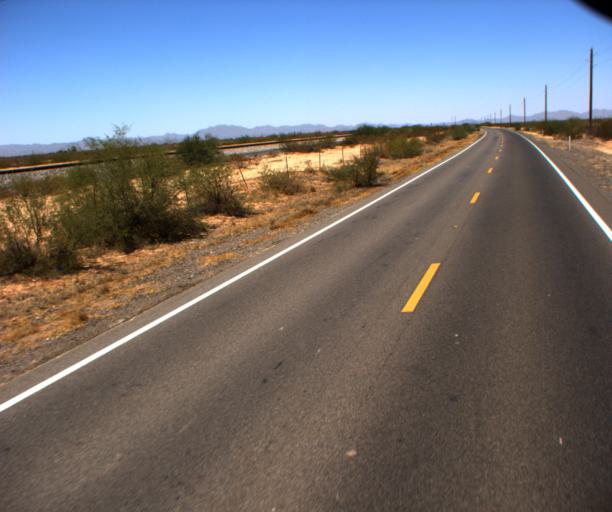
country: US
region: Arizona
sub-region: Pinal County
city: Maricopa
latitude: 33.0703
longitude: -112.2124
